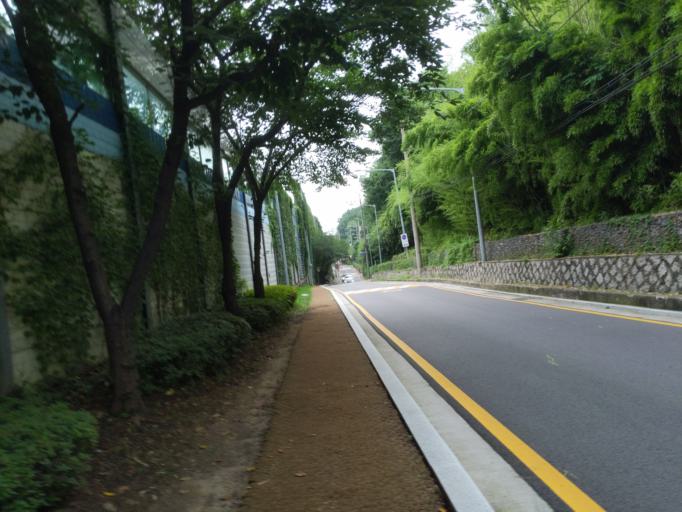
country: KR
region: Seoul
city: Seoul
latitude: 37.5059
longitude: 127.0176
